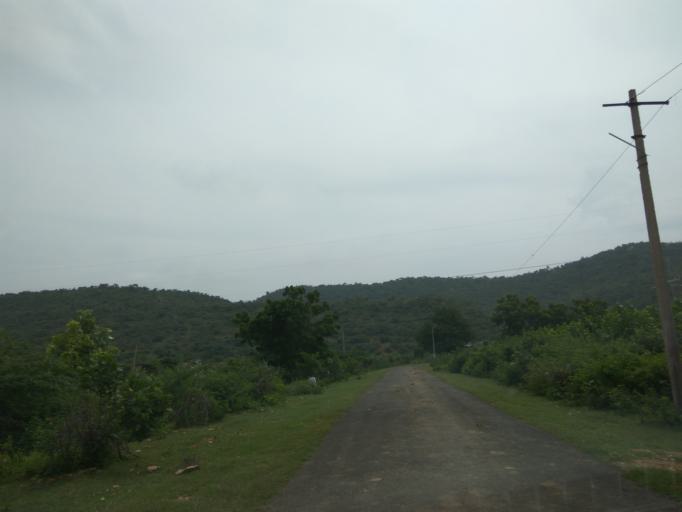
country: IN
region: Andhra Pradesh
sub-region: Prakasam
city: Cumbum
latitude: 15.4449
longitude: 79.0802
